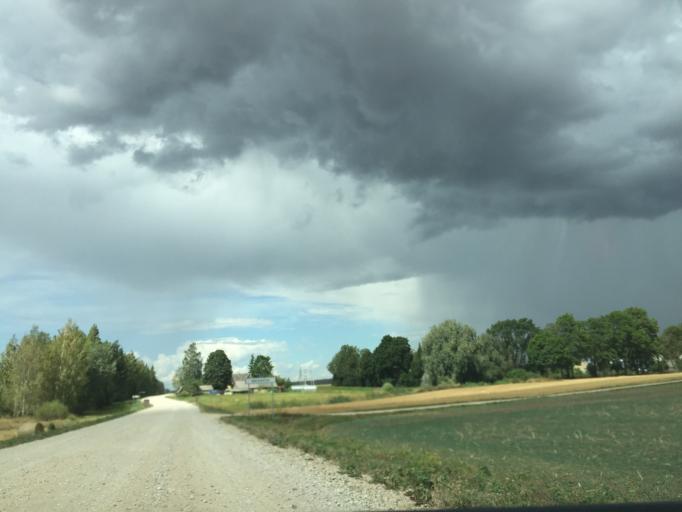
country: LT
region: Siauliu apskritis
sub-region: Joniskis
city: Joniskis
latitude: 56.2833
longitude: 23.7233
